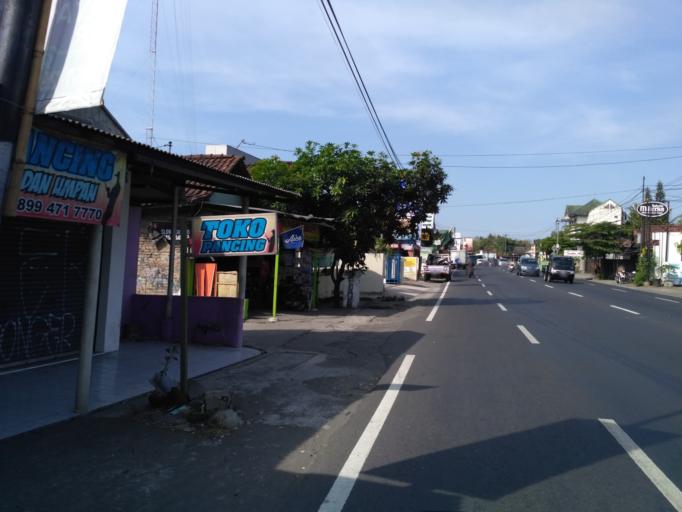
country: ID
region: Daerah Istimewa Yogyakarta
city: Godean
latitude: -7.8122
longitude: 110.2716
